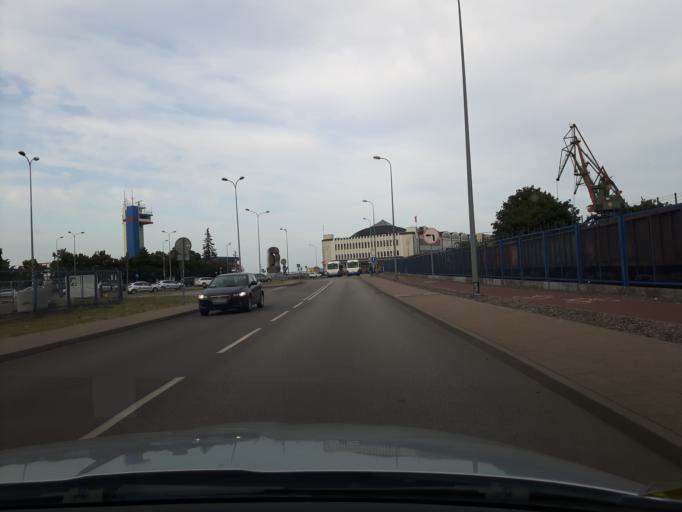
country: PL
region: Pomeranian Voivodeship
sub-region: Gdynia
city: Gdynia
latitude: 54.5321
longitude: 18.5454
